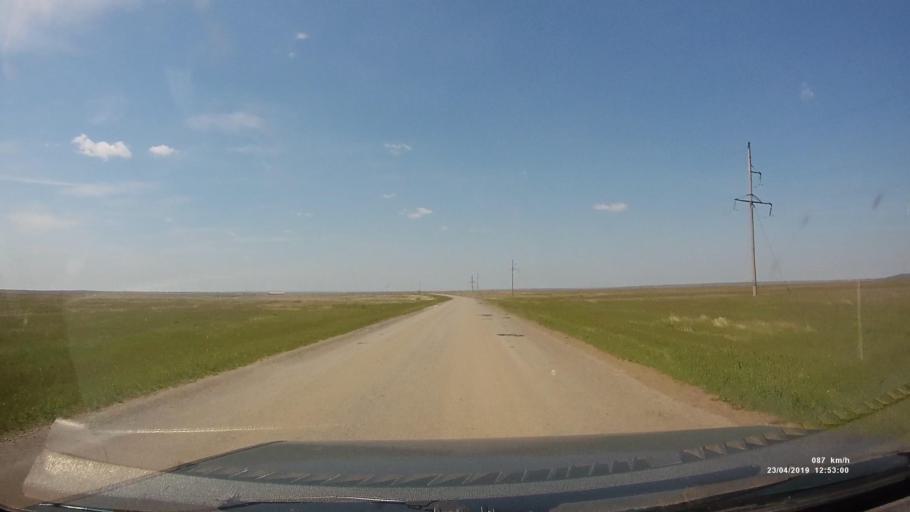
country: RU
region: Kalmykiya
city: Yashalta
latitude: 46.5701
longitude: 42.6020
